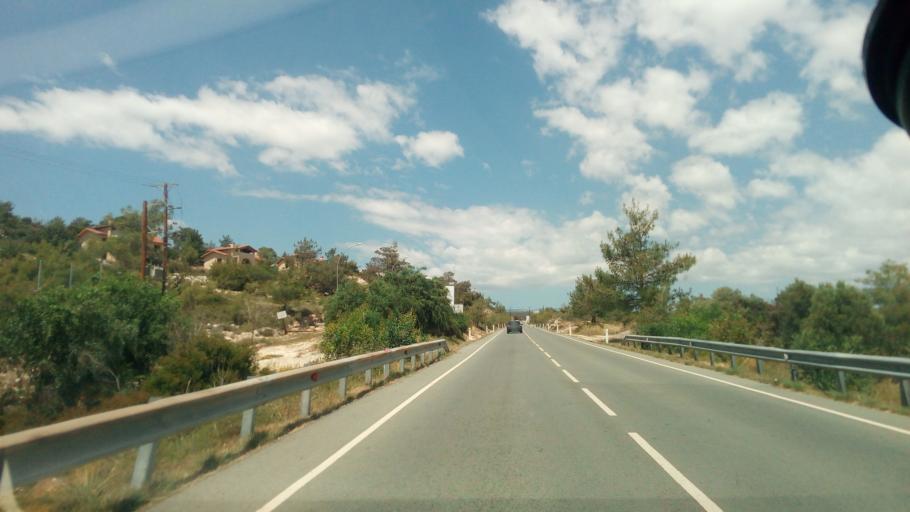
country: CY
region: Limassol
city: Sotira
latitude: 34.7165
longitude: 32.8921
